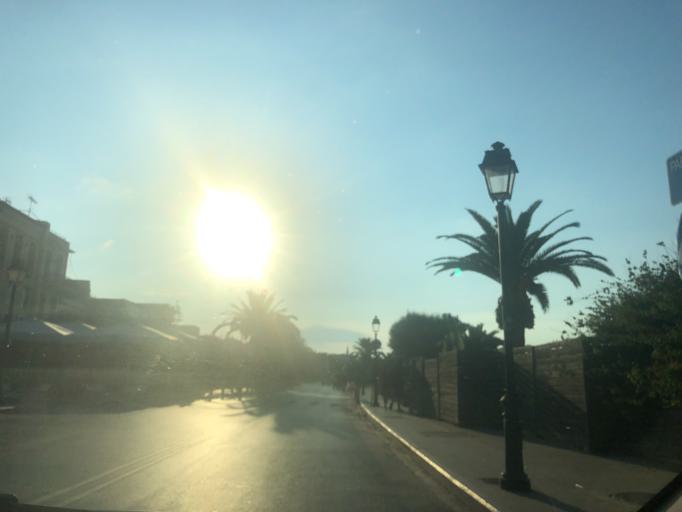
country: GR
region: Crete
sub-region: Nomos Rethymnis
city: Rethymno
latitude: 35.3670
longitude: 24.4802
